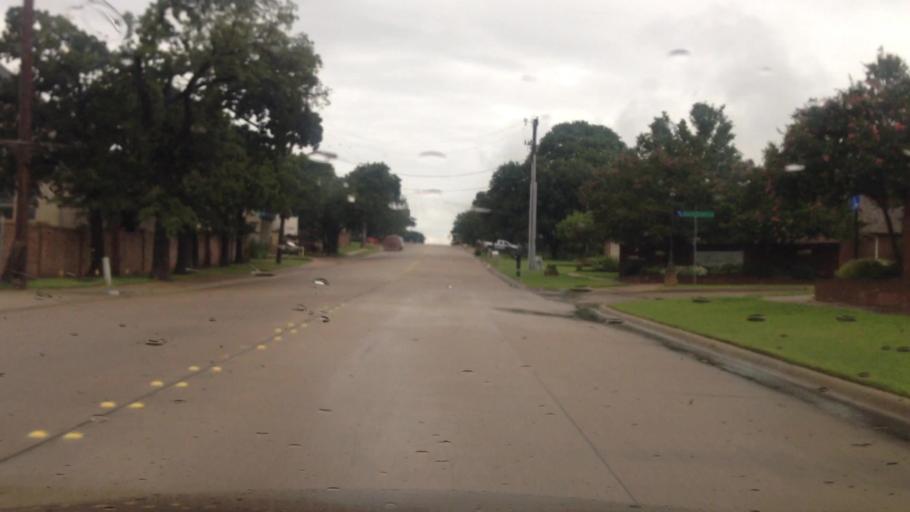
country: US
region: Texas
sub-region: Tarrant County
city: Colleyville
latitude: 32.8689
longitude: -97.1918
